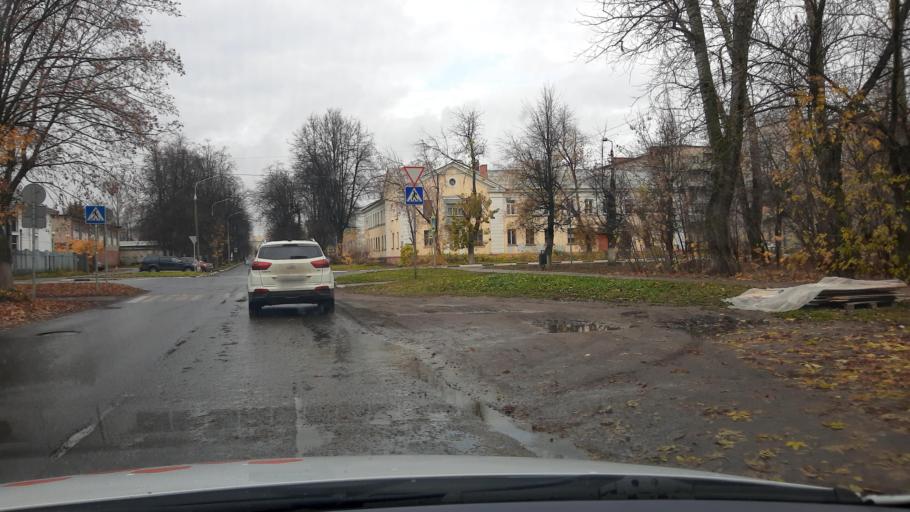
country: RU
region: Moskovskaya
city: Elektrostal'
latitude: 55.7787
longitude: 38.4497
